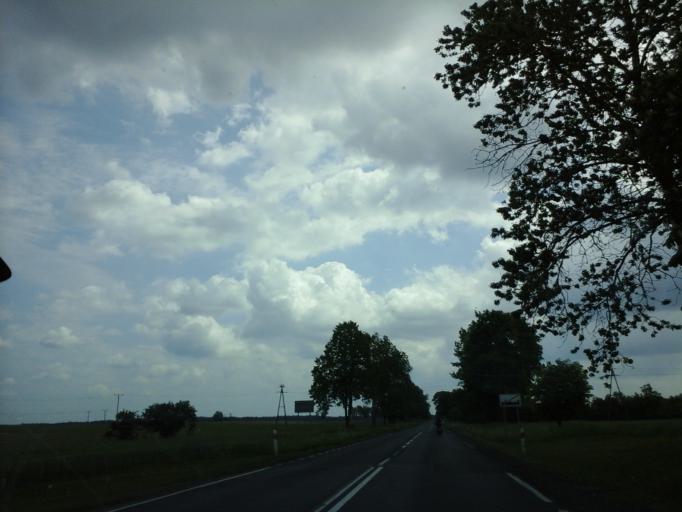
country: PL
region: West Pomeranian Voivodeship
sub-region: Powiat drawski
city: Kalisz Pomorski
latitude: 53.2980
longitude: 15.9216
